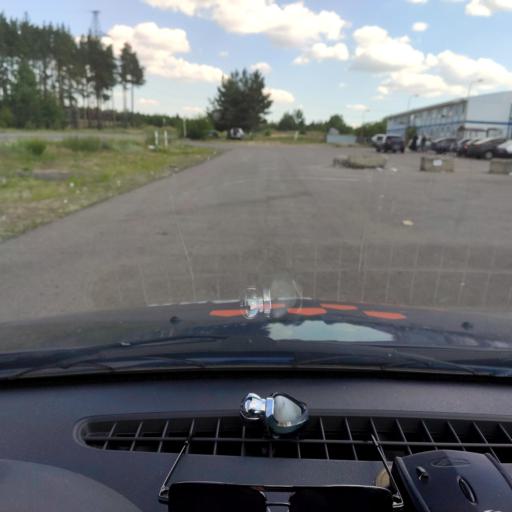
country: RU
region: Voronezj
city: Novovoronezh
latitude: 51.3294
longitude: 39.2548
